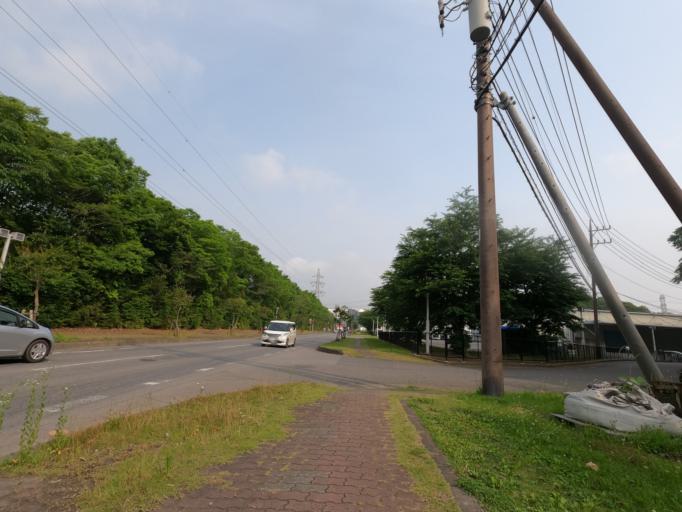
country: JP
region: Ibaraki
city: Moriya
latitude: 35.9543
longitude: 139.9637
